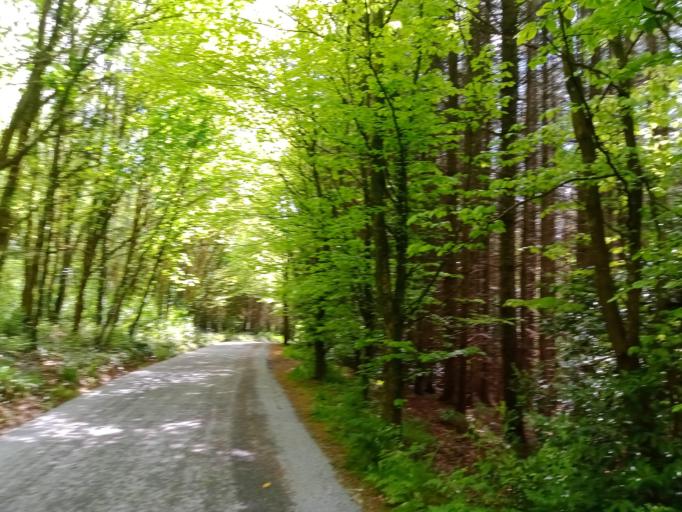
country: IE
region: Leinster
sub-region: Kilkenny
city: Castlecomer
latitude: 52.8122
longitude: -7.2019
